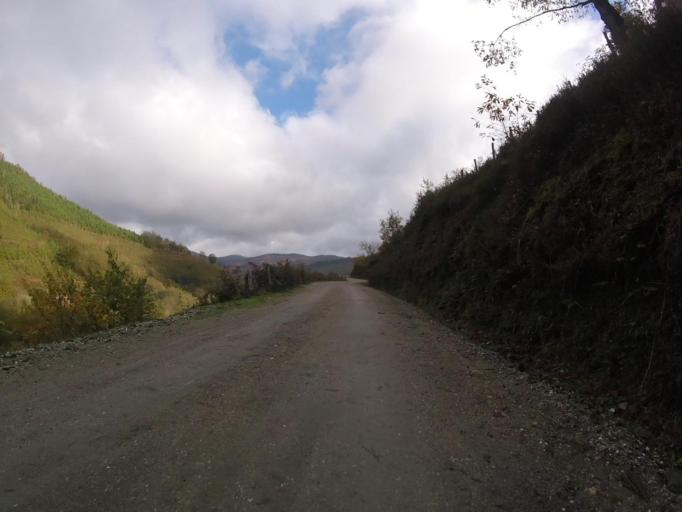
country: ES
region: Navarre
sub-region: Provincia de Navarra
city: Goizueta
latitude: 43.2117
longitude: -1.8406
